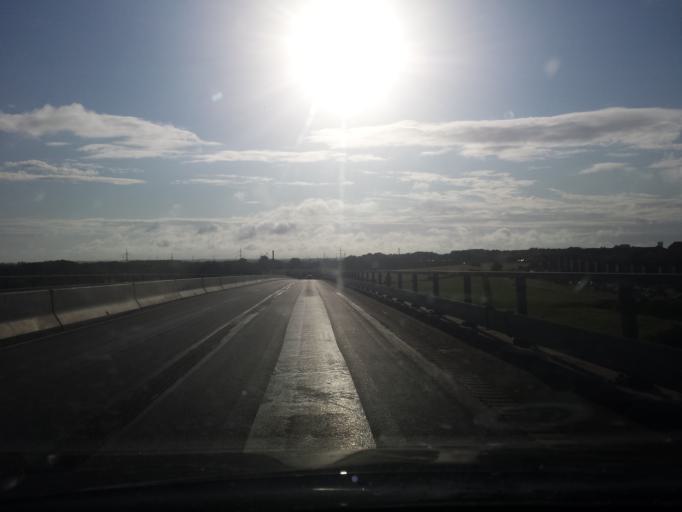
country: DK
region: South Denmark
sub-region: Sonderborg Kommune
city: Dybbol
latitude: 54.9223
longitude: 9.7683
